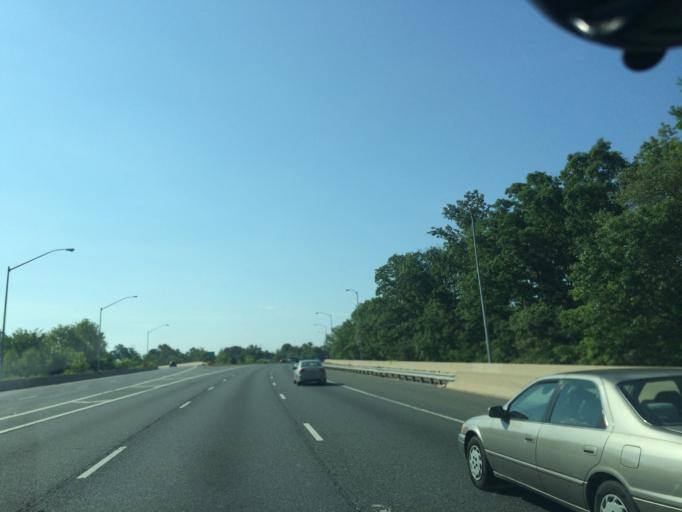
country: US
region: Maryland
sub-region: Baltimore County
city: Carney
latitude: 39.3839
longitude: -76.5231
